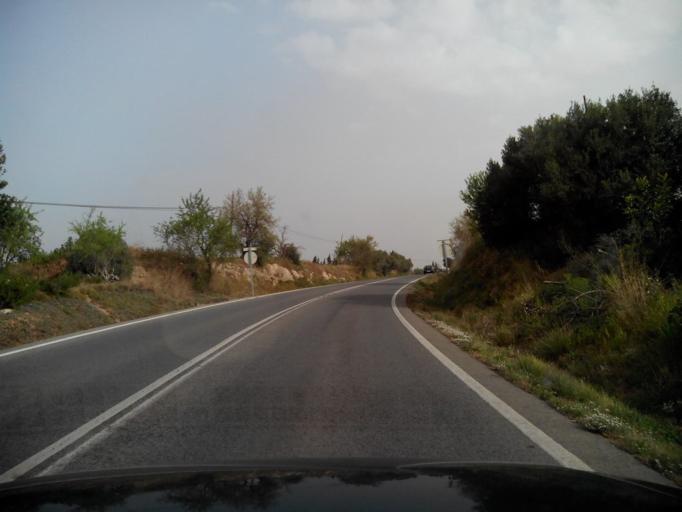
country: ES
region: Catalonia
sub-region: Provincia de Tarragona
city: Reus
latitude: 41.1250
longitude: 1.0967
